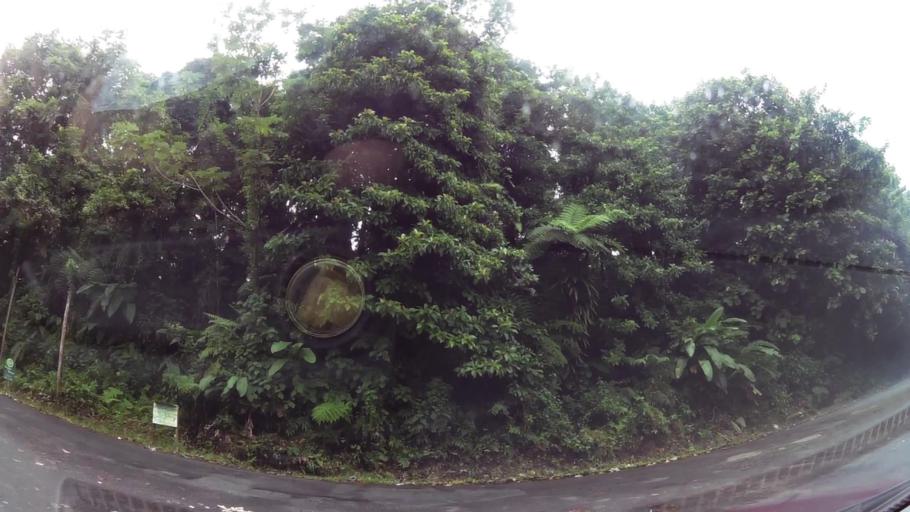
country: DM
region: Saint Paul
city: Pont Casse
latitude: 15.3903
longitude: -61.3110
